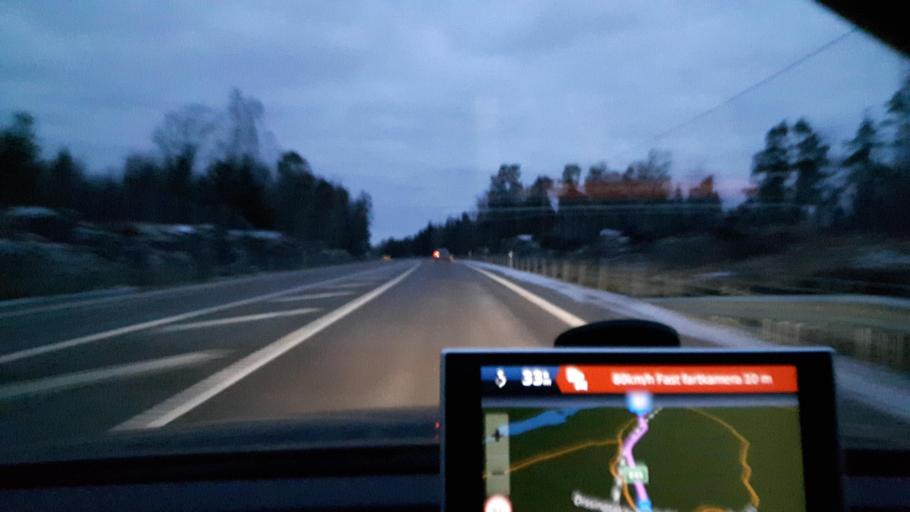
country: SE
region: Vaestra Goetaland
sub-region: Vanersborgs Kommun
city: Vanersborg
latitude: 58.4421
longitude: 12.2828
